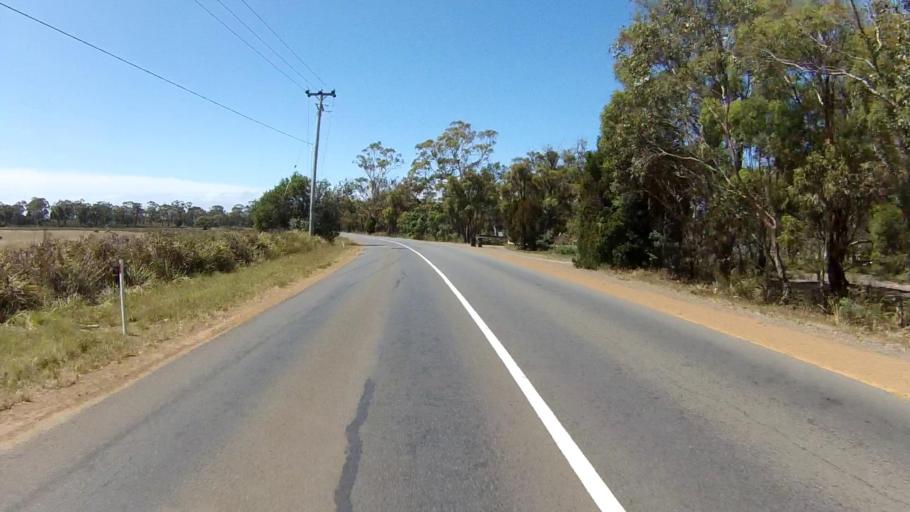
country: AU
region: Tasmania
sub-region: Clarence
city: Sandford
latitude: -42.9417
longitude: 147.4872
